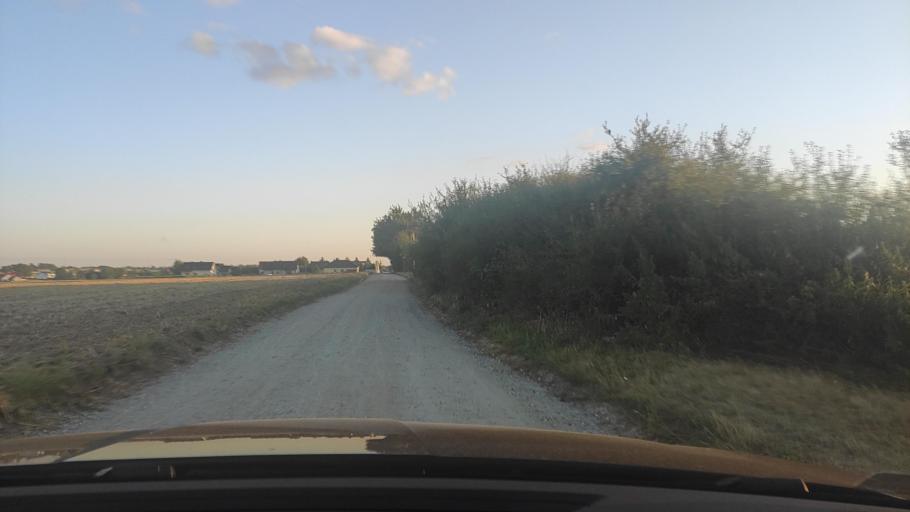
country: PL
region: Greater Poland Voivodeship
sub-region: Powiat poznanski
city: Swarzedz
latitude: 52.4341
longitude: 17.1167
